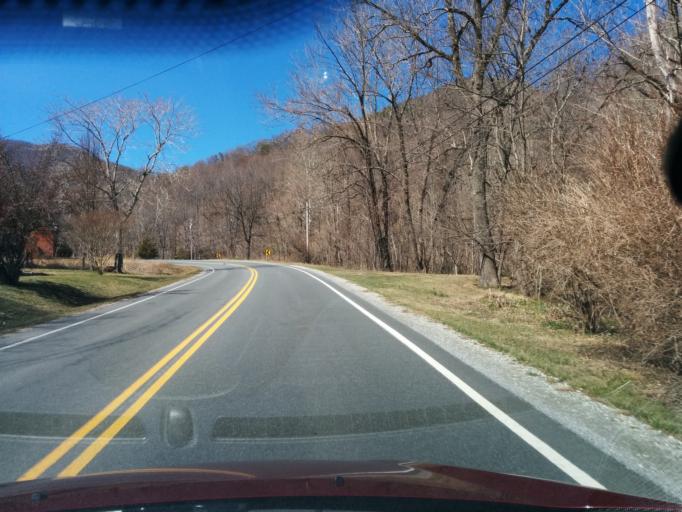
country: US
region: Virginia
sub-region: Nelson County
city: Nellysford
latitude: 37.8807
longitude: -78.9627
